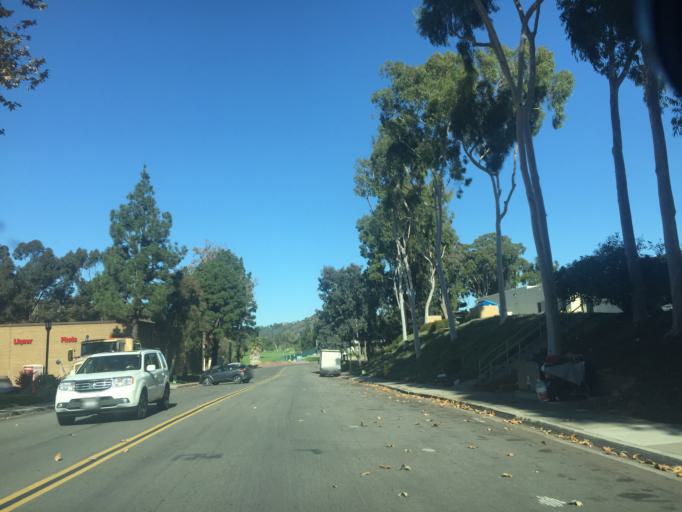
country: US
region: California
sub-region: San Diego County
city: La Mesa
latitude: 32.7915
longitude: -117.0996
